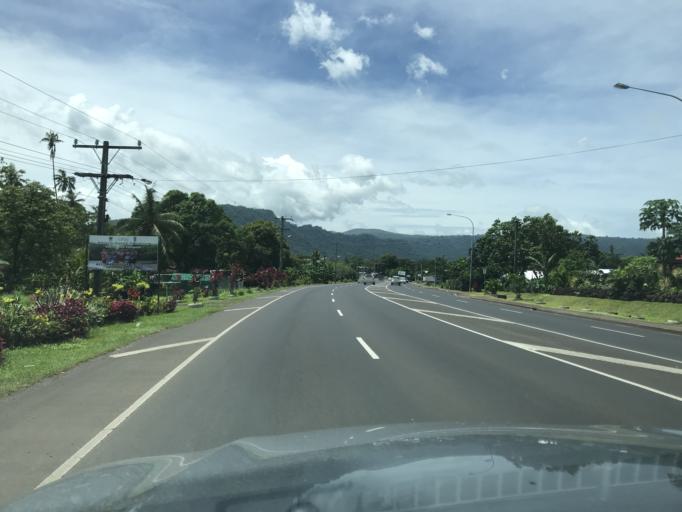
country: WS
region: Tuamasaga
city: Vaiusu
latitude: -13.8285
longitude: -171.7923
